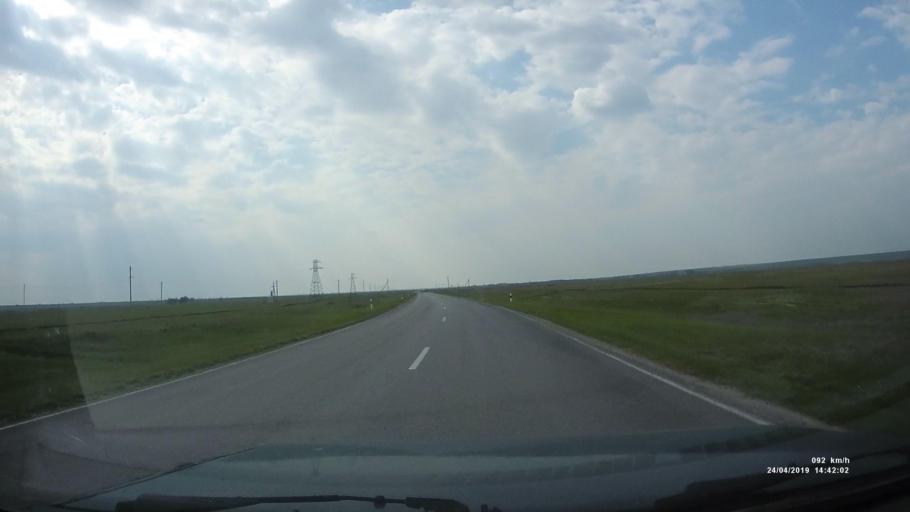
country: RU
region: Rostov
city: Remontnoye
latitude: 46.4499
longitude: 43.8699
